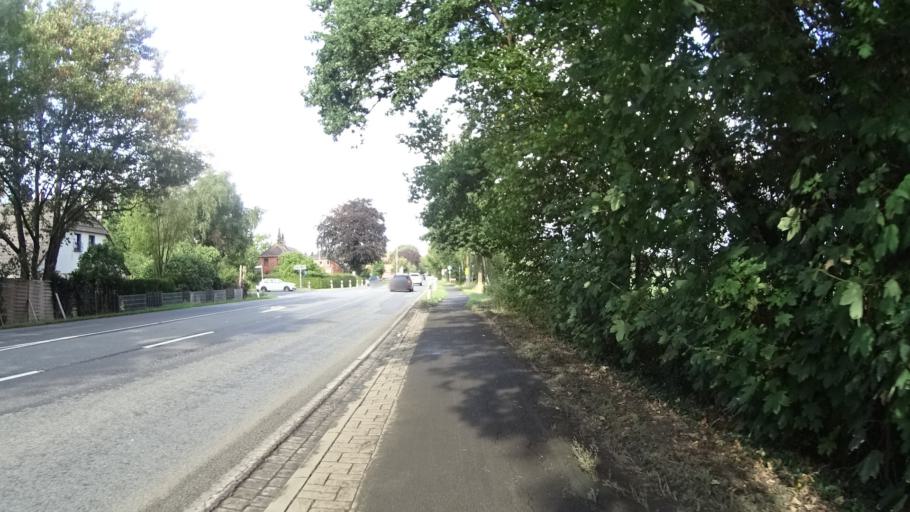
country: DE
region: Lower Saxony
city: Varel
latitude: 53.3919
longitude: 8.1702
